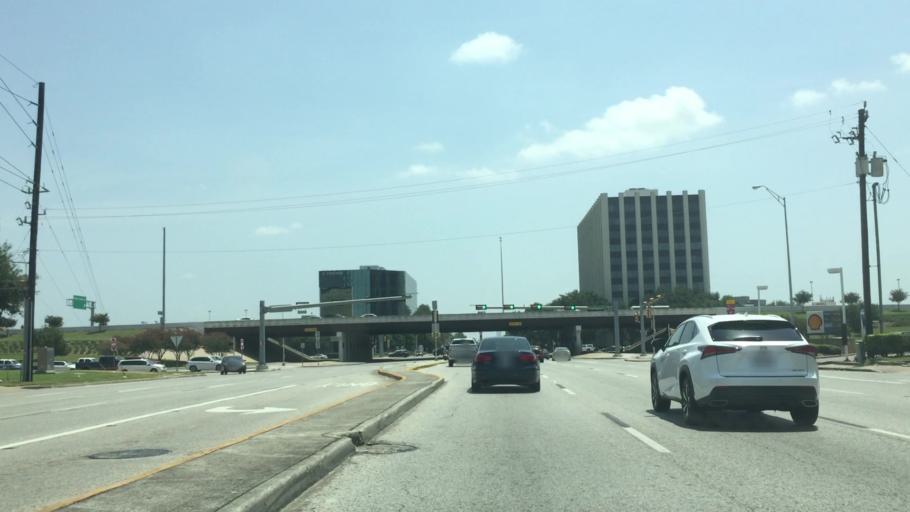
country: US
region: Texas
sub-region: Harris County
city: Bunker Hill Village
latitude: 29.7369
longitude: -95.5595
